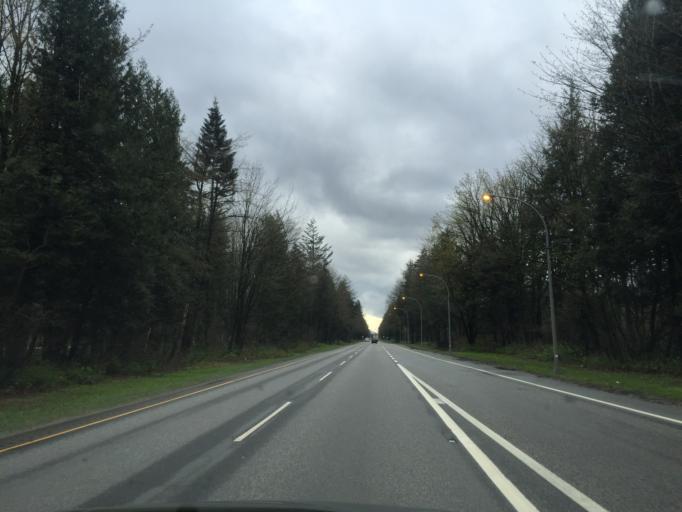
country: CA
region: British Columbia
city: Hope
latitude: 49.3440
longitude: -121.5944
